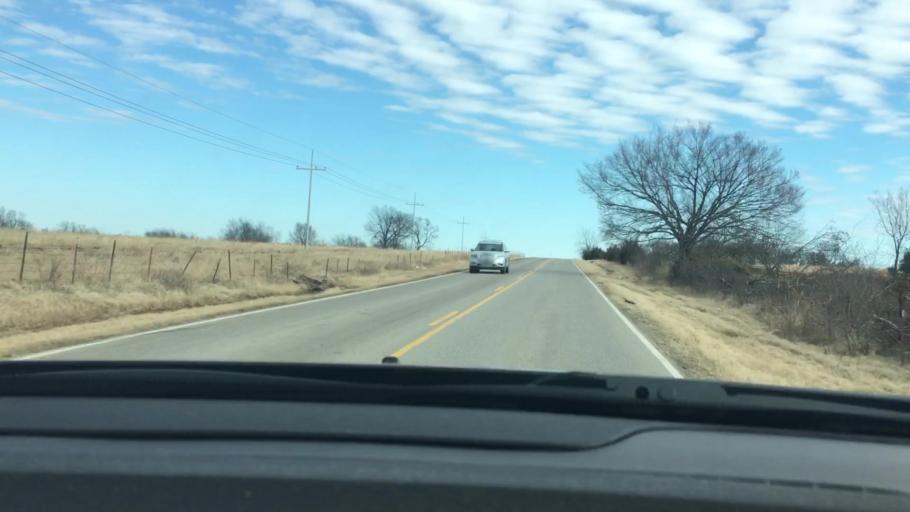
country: US
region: Oklahoma
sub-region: Garvin County
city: Stratford
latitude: 34.7966
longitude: -96.9281
